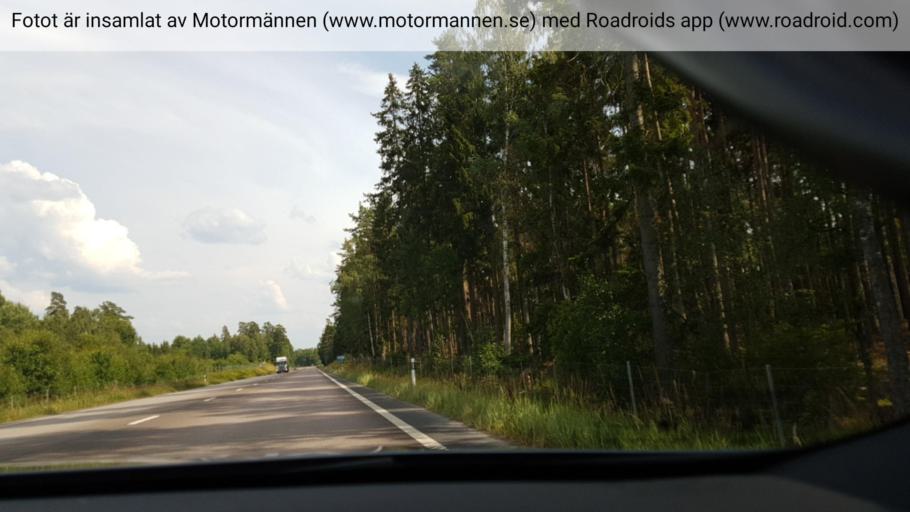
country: SE
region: Vaestra Goetaland
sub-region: Lidkopings Kommun
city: Vinninga
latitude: 58.4248
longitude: 13.3344
